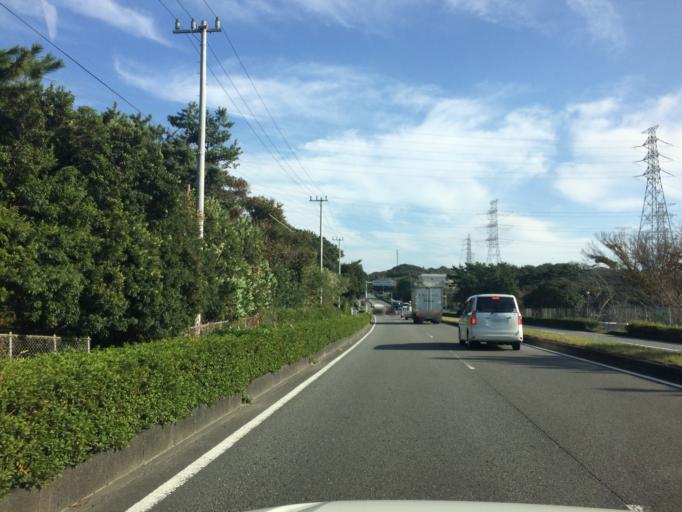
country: JP
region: Shizuoka
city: Oyama
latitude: 34.6292
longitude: 138.1436
